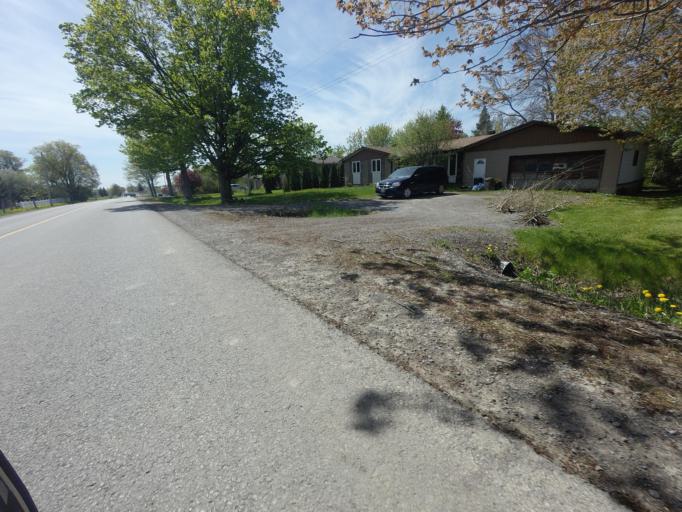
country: CA
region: Ontario
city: Arnprior
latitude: 45.3989
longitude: -76.1508
